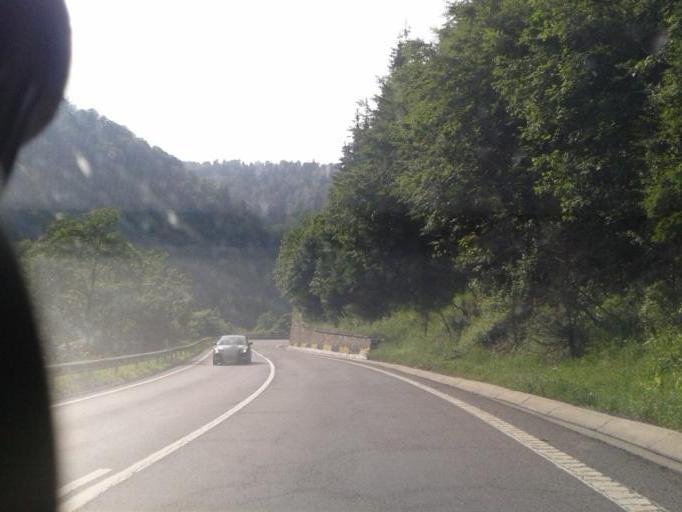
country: RO
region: Prahova
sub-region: Oras Azuga
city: Azuga
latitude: 45.4657
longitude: 25.5629
